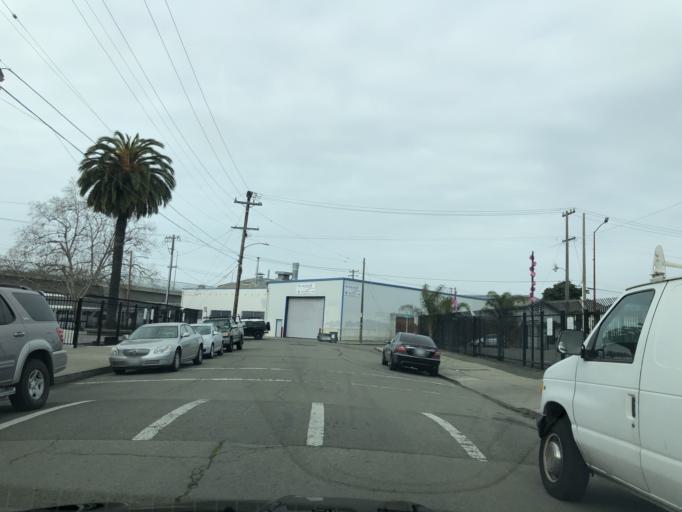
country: US
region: California
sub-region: Alameda County
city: Alameda
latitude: 37.7778
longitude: -122.2357
